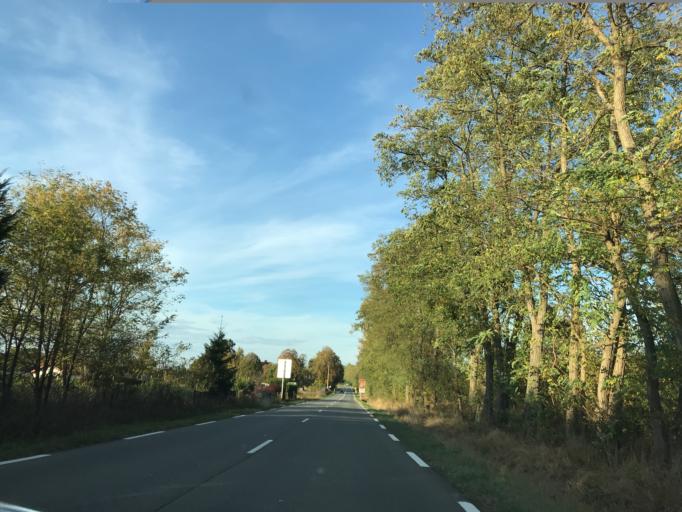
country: FR
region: Auvergne
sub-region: Departement du Puy-de-Dome
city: Puy-Guillaume
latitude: 45.9810
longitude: 3.4840
